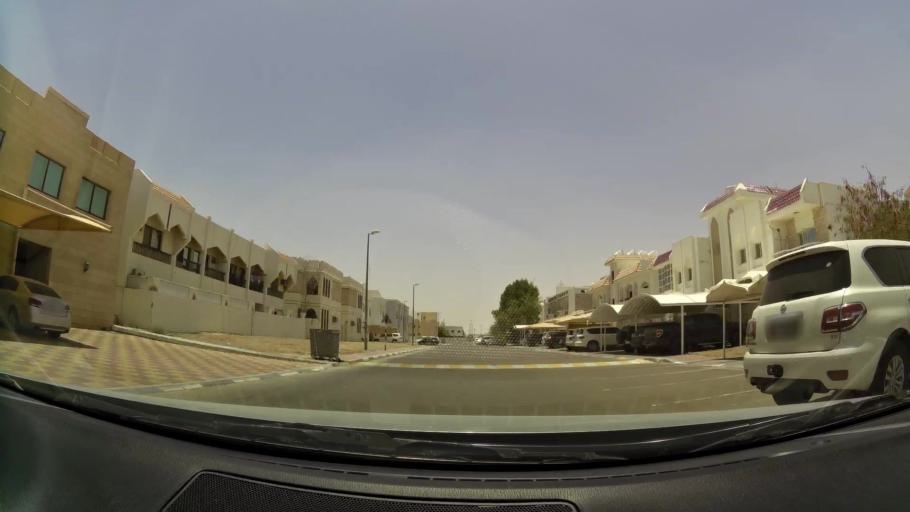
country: OM
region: Al Buraimi
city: Al Buraymi
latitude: 24.2617
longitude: 55.7240
